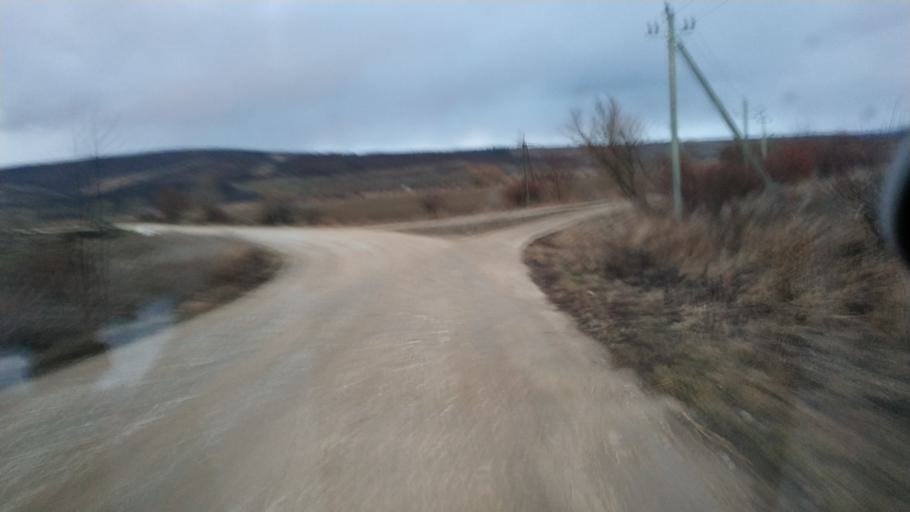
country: MD
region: Taraclia
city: Telenesti
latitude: 47.3891
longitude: 28.3313
